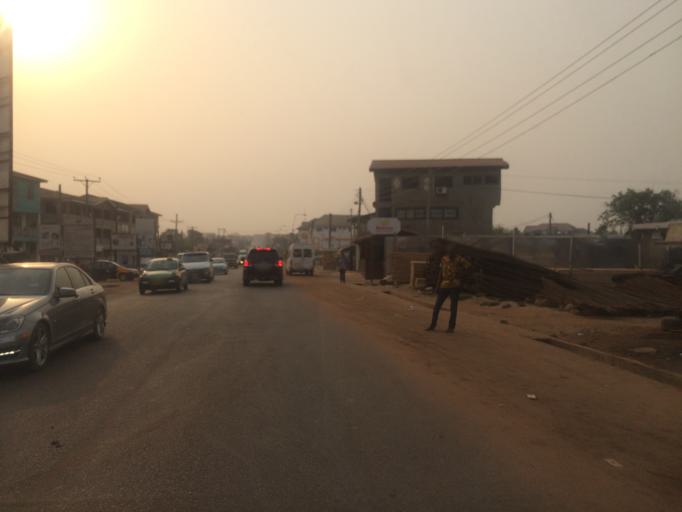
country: GH
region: Greater Accra
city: Nungua
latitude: 5.6426
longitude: -0.1101
